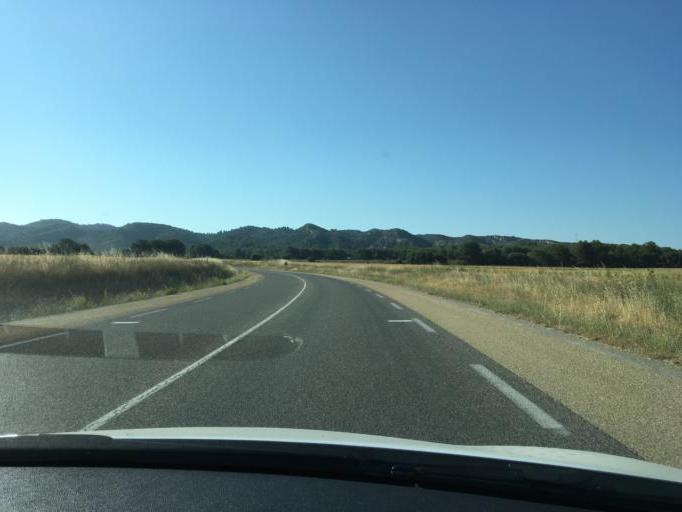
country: FR
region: Provence-Alpes-Cote d'Azur
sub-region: Departement des Bouches-du-Rhone
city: Charleval
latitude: 43.7131
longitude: 5.2256
